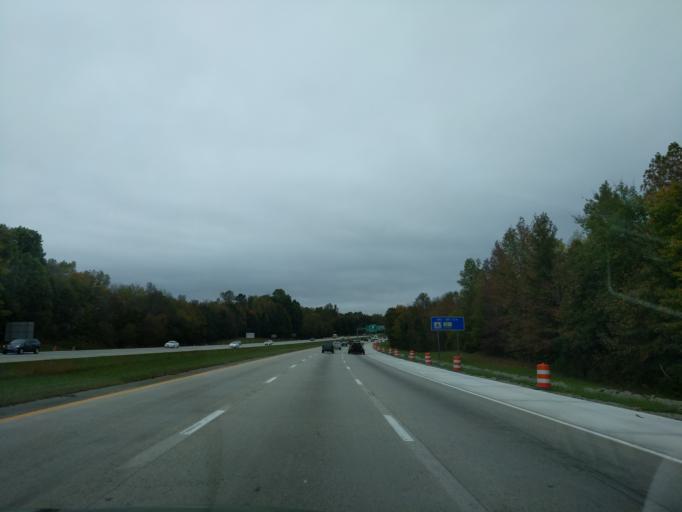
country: US
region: North Carolina
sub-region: Randolph County
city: Archdale
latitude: 35.9113
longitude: -79.9496
